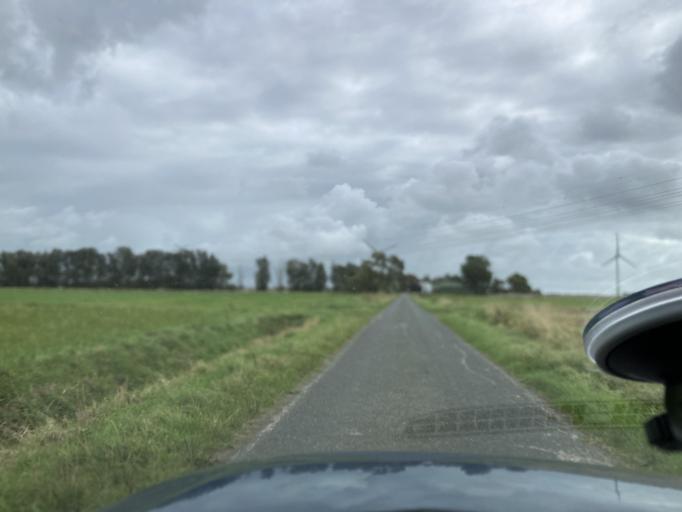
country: DE
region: Schleswig-Holstein
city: Oesterwurth
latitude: 54.1967
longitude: 8.9663
